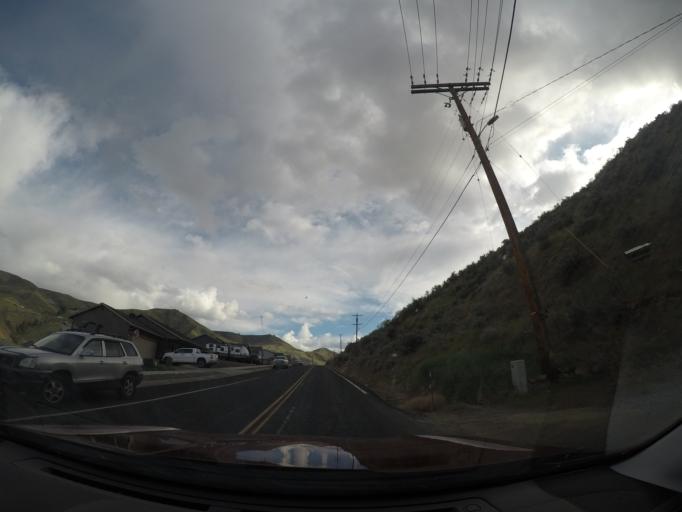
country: US
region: Washington
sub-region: Chelan County
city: South Wenatchee
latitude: 47.3892
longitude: -120.3101
